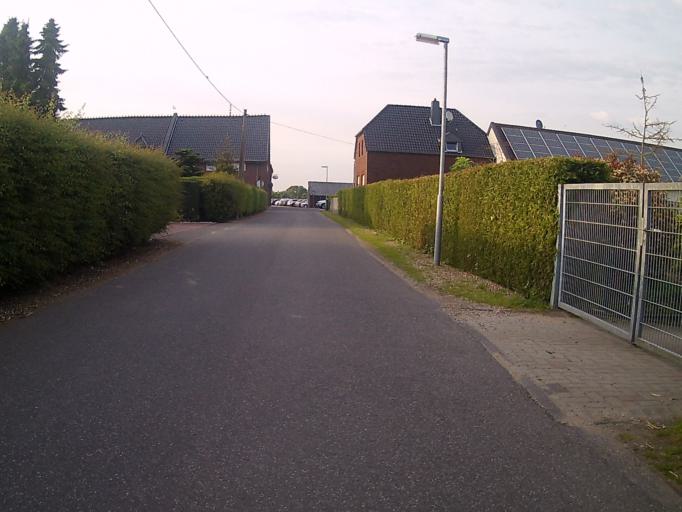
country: DE
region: North Rhine-Westphalia
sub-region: Regierungsbezirk Dusseldorf
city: Krefeld
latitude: 51.4019
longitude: 6.5260
